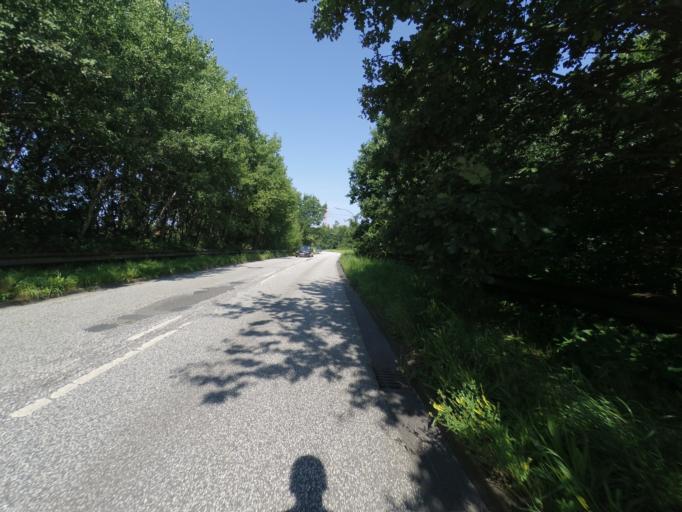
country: DE
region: Hamburg
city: Wandsbek
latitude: 53.5202
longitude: 10.1210
